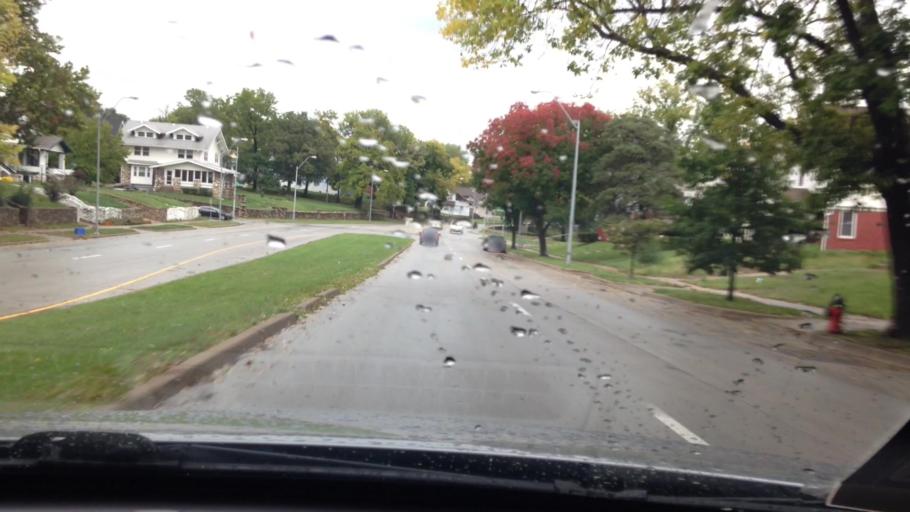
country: US
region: Missouri
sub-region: Jackson County
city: Kansas City
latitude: 39.0729
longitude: -94.5666
